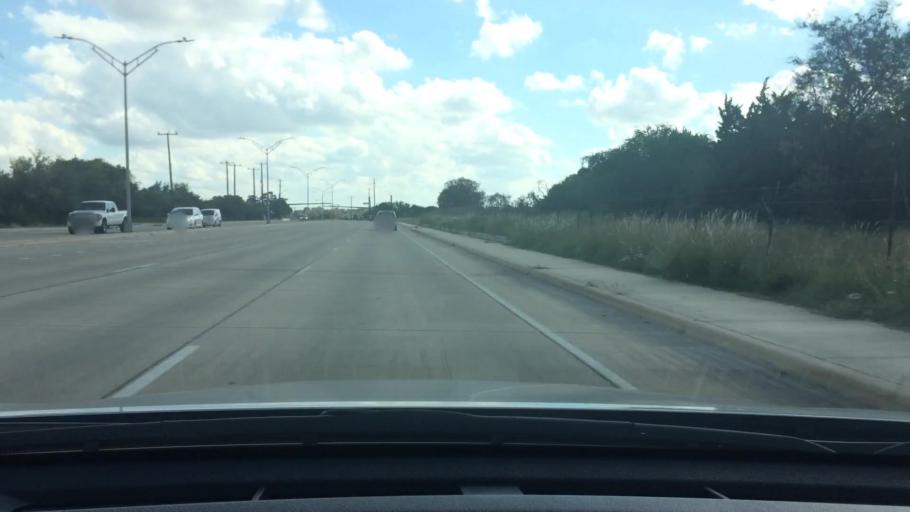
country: US
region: Texas
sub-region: Bexar County
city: Hollywood Park
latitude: 29.6192
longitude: -98.4229
